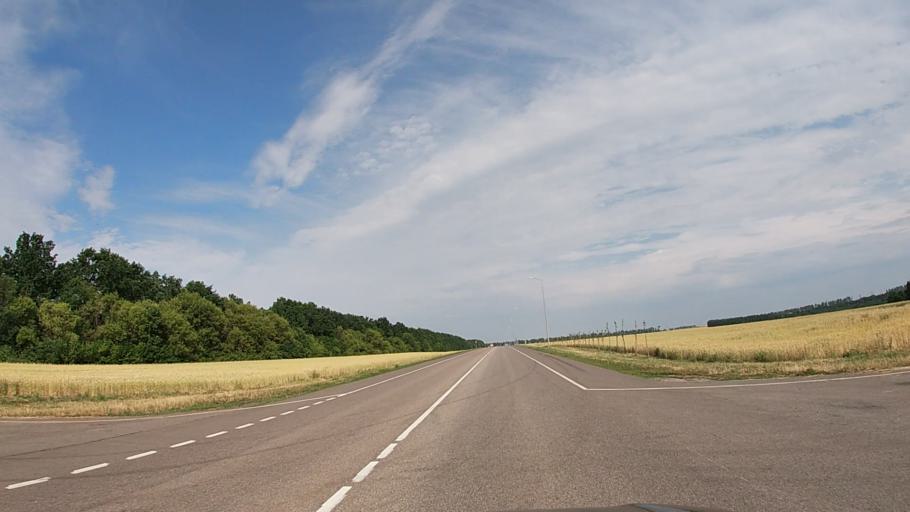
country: RU
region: Belgorod
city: Proletarskiy
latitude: 50.8252
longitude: 35.7815
